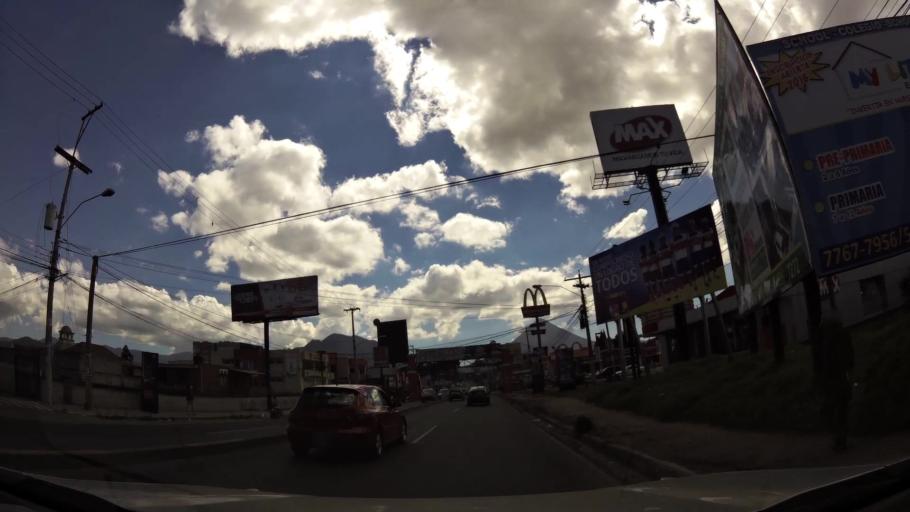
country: GT
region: Quetzaltenango
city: Quetzaltenango
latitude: 14.8534
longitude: -91.5368
